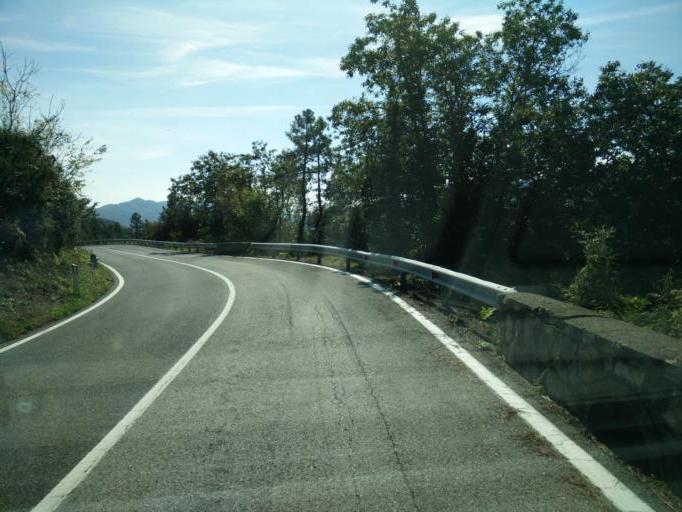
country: IT
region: Liguria
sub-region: Provincia di La Spezia
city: Carrodano
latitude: 44.2506
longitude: 9.6041
